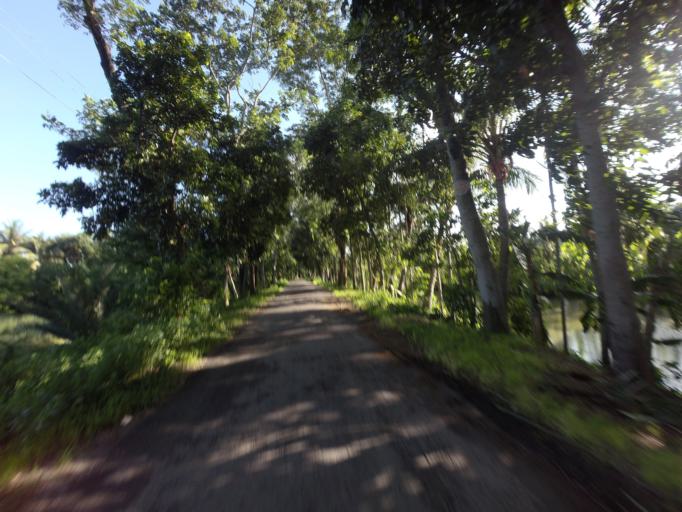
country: BD
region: Khulna
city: Kalia
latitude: 22.9538
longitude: 89.5503
